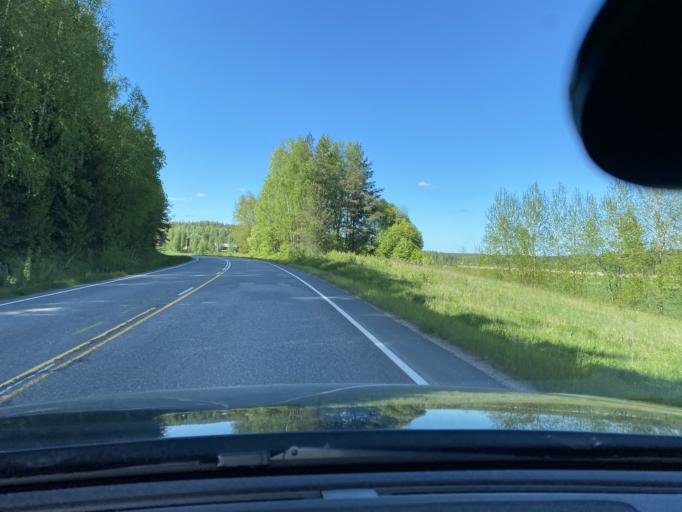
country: FI
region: Varsinais-Suomi
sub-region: Turku
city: Sauvo
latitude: 60.3743
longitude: 22.6705
